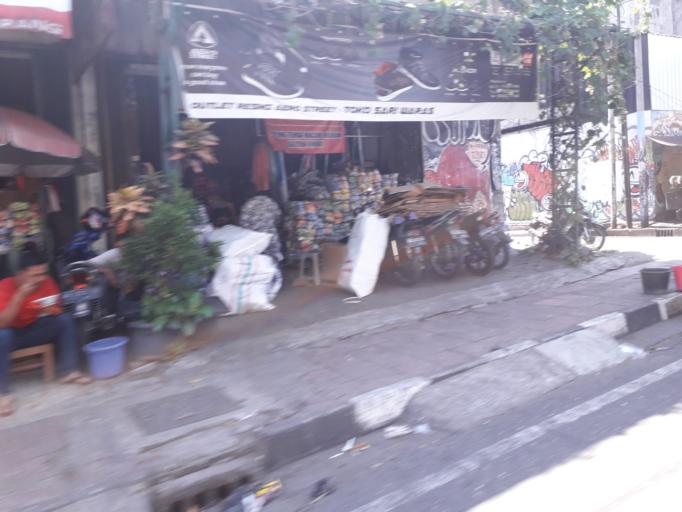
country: ID
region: Daerah Istimewa Yogyakarta
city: Yogyakarta
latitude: -7.8001
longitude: 110.3693
